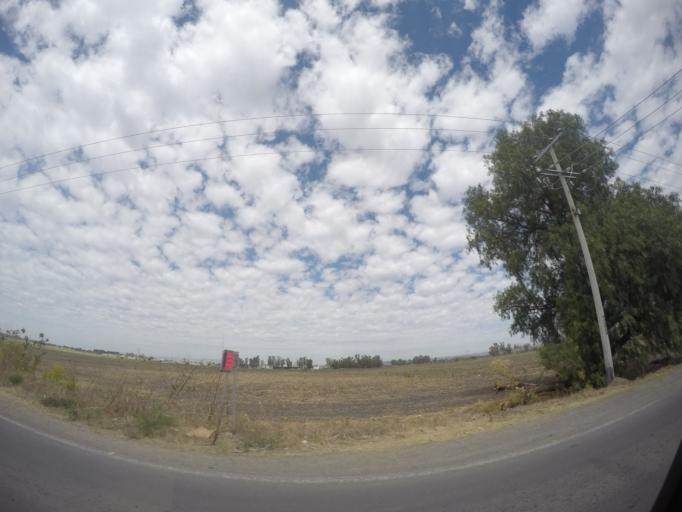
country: MX
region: Guanajuato
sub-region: Leon
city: Colonia Latinoamericana
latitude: 21.0326
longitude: -101.6948
